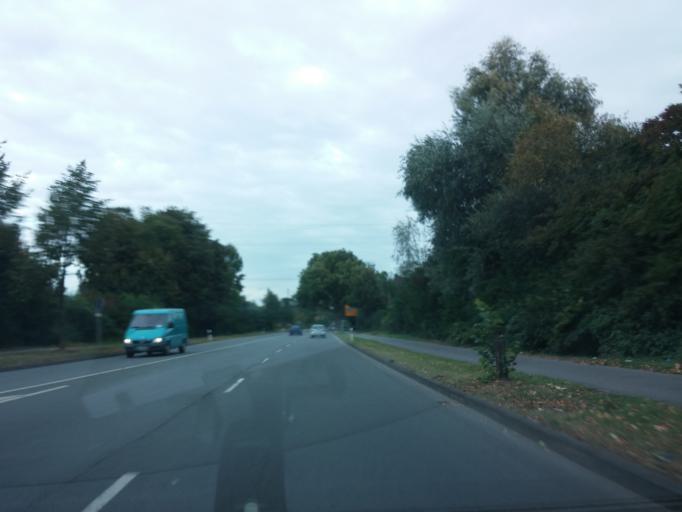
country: DE
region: North Rhine-Westphalia
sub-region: Regierungsbezirk Munster
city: Gelsenkirchen
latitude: 51.5212
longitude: 7.1320
